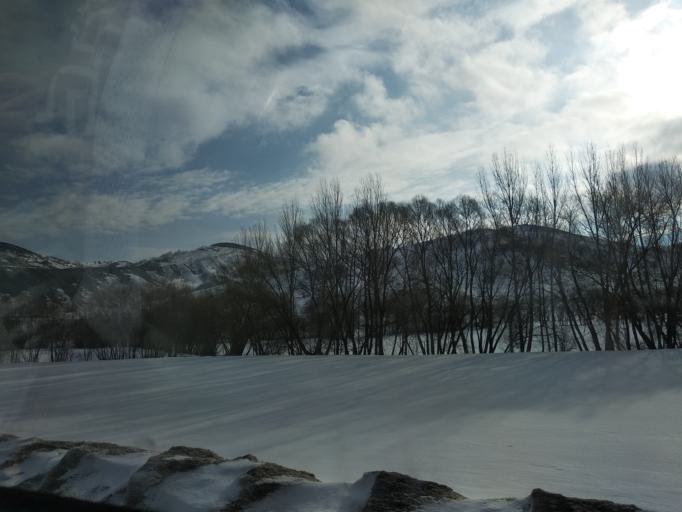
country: TR
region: Erzincan
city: Catalarmut
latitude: 39.9085
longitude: 39.4053
